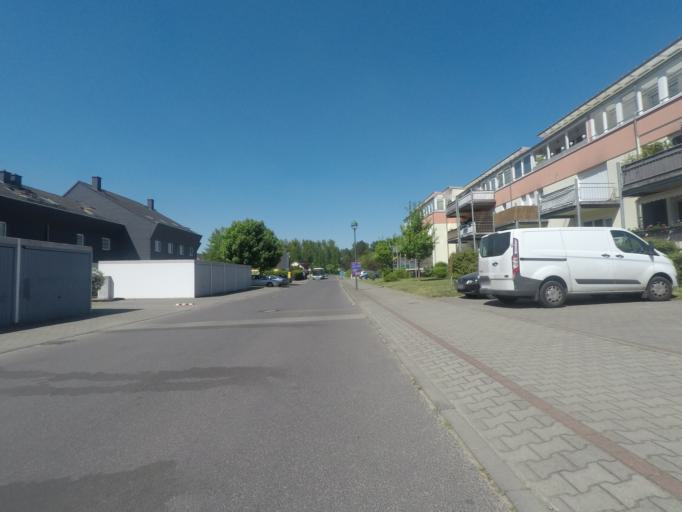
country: DE
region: Brandenburg
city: Melchow
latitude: 52.8509
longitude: 13.6949
